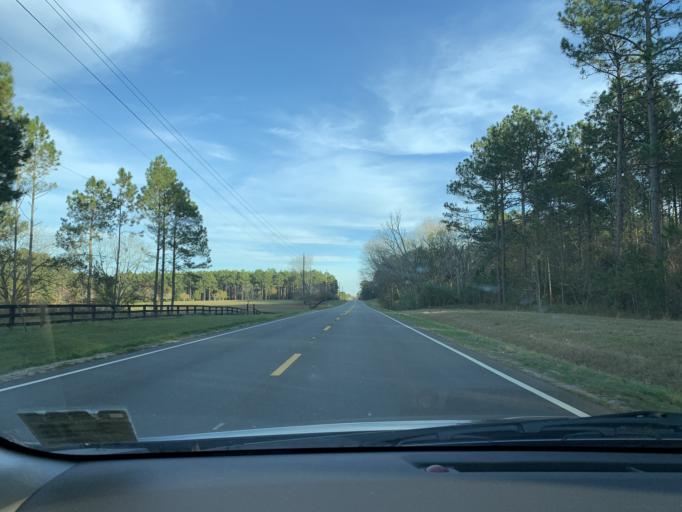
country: US
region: Georgia
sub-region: Irwin County
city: Ocilla
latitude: 31.5836
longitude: -83.0716
